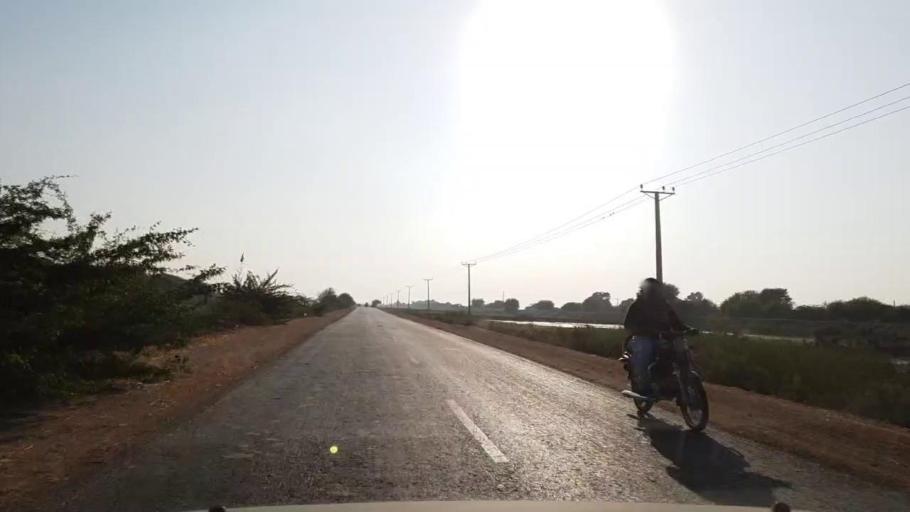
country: PK
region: Sindh
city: Mirpur Batoro
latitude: 24.7713
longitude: 68.2813
